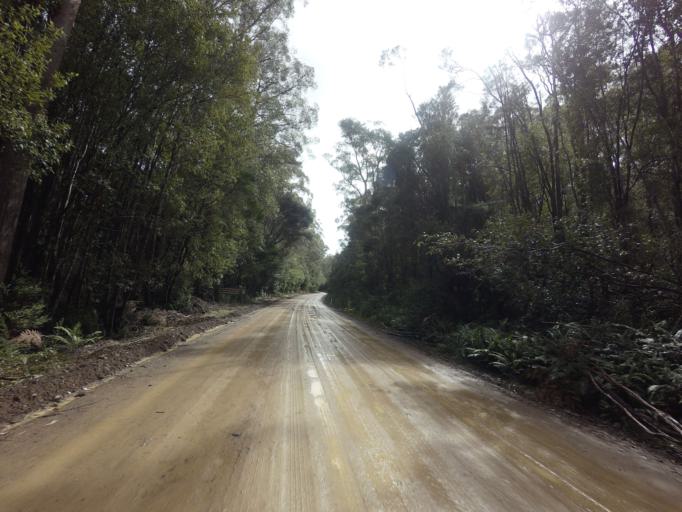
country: AU
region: Tasmania
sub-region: Huon Valley
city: Geeveston
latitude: -43.4110
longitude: 146.8730
